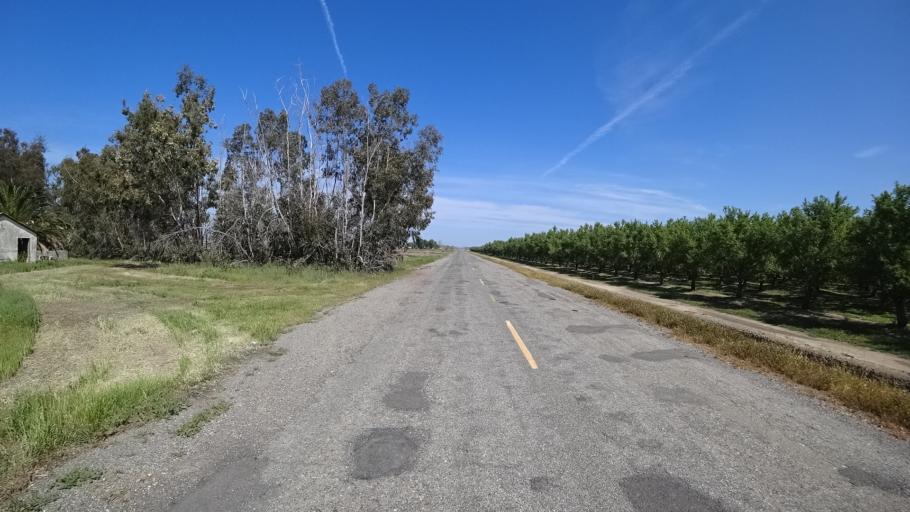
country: US
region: California
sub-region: Glenn County
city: Hamilton City
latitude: 39.6098
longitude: -122.0463
